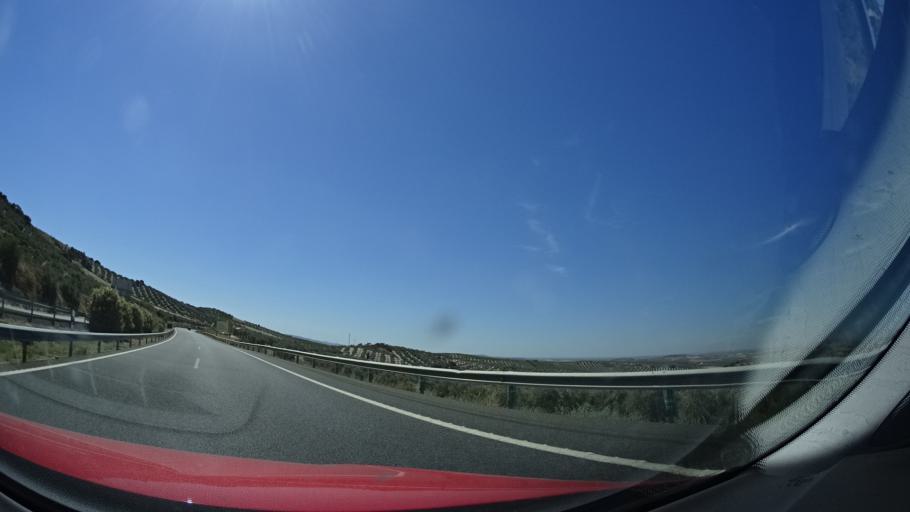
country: ES
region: Andalusia
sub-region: Provincia de Sevilla
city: Estepa
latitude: 37.2869
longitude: -4.9116
